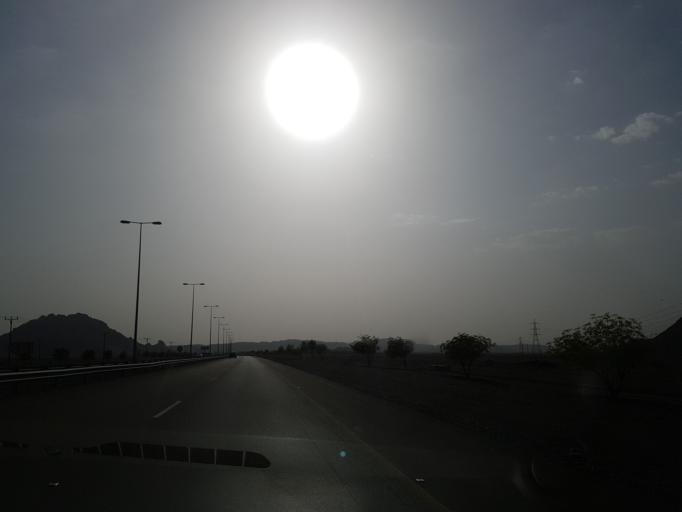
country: OM
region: Al Buraimi
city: Al Buraymi
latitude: 24.2462
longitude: 56.0015
